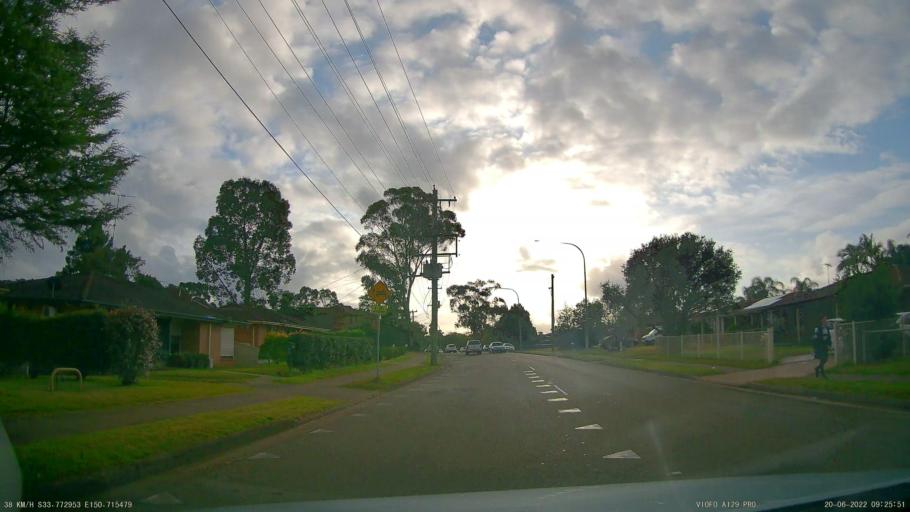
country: AU
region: New South Wales
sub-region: Penrith Municipality
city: Kingswood Park
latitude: -33.7729
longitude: 150.7157
